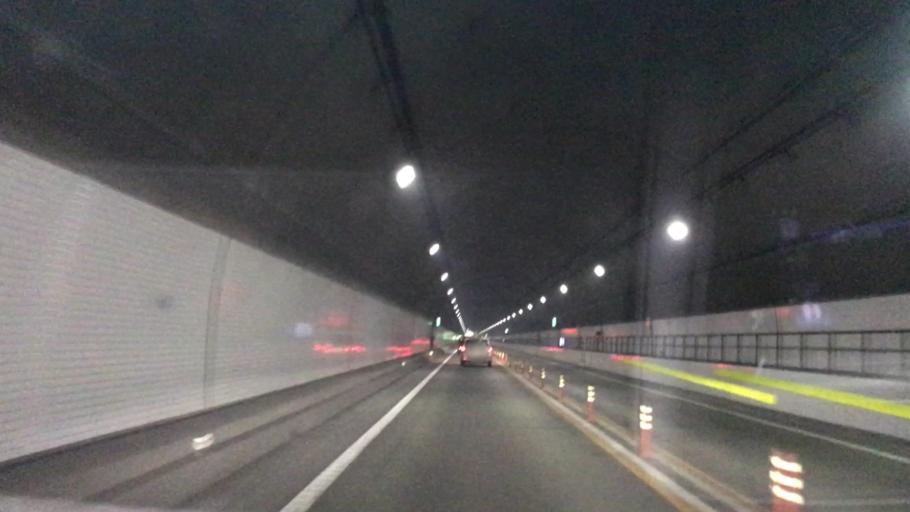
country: JP
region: Hokkaido
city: Shimo-furano
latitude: 42.9539
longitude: 142.3156
